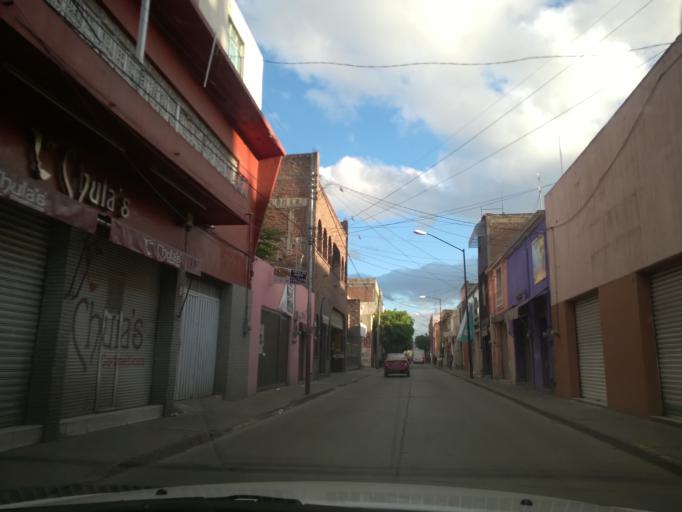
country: MX
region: Guanajuato
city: Leon
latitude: 21.1248
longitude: -101.6844
